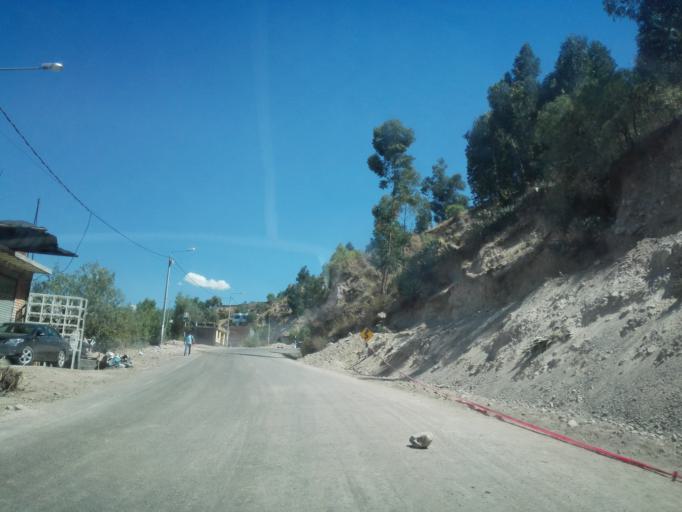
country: PE
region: Ayacucho
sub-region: Provincia de Huamanga
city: Ayacucho
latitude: -13.1615
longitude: -74.2395
